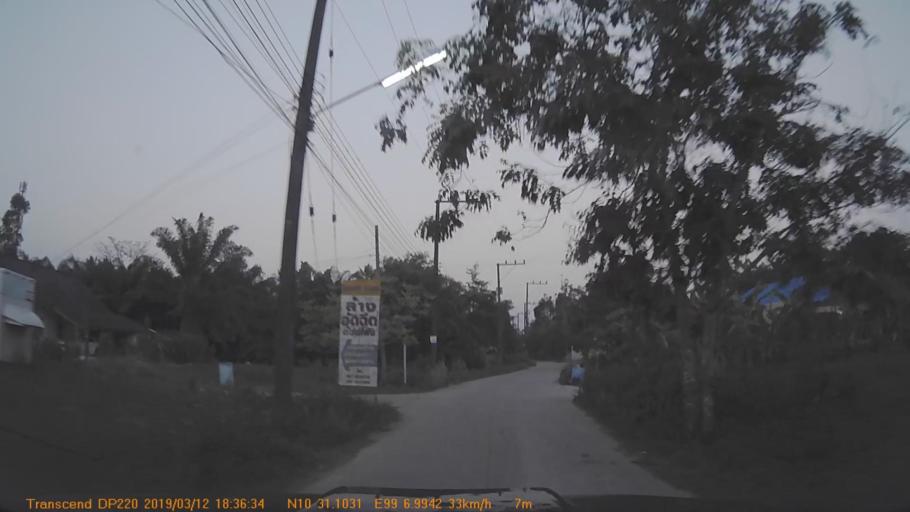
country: TH
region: Chumphon
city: Chumphon
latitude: 10.5183
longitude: 99.1168
